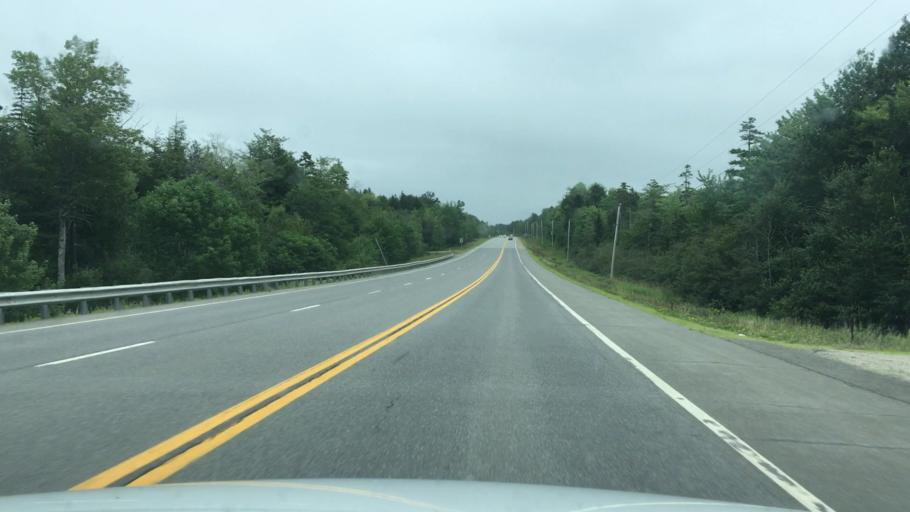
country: US
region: Maine
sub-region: Hancock County
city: Franklin
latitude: 44.8265
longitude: -68.1172
